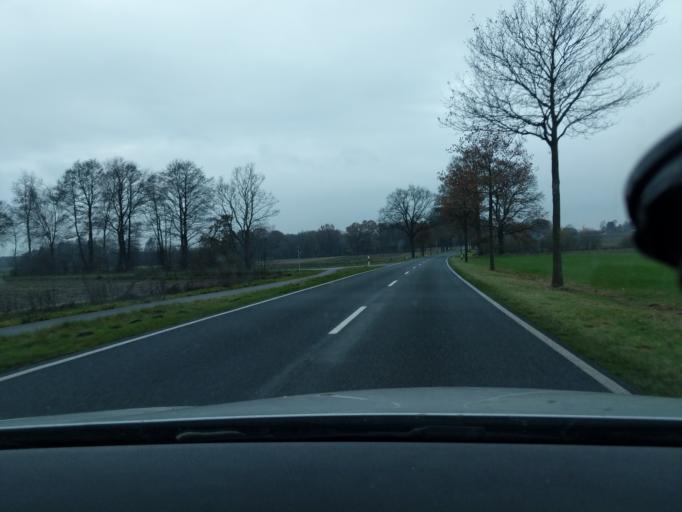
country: DE
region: Lower Saxony
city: Heeslingen
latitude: 53.3410
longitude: 9.3856
